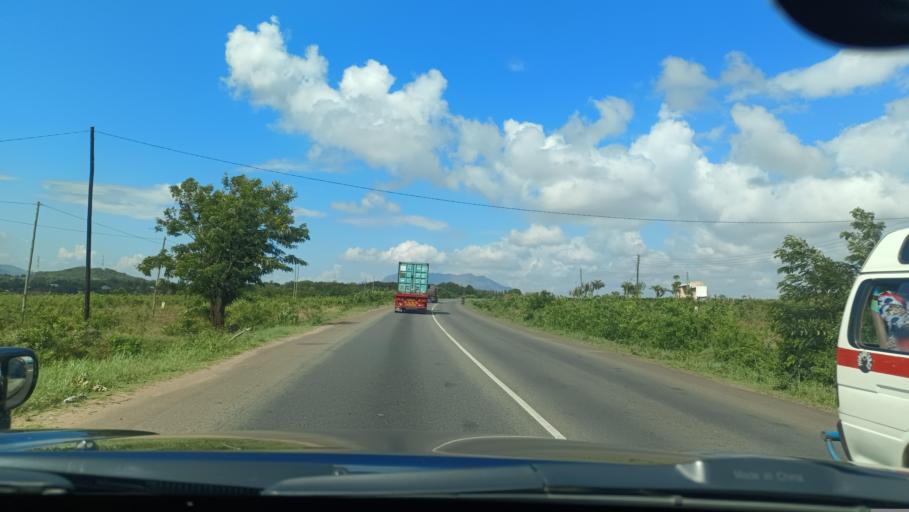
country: TZ
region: Morogoro
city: Morogoro
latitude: -6.8004
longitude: 37.7170
